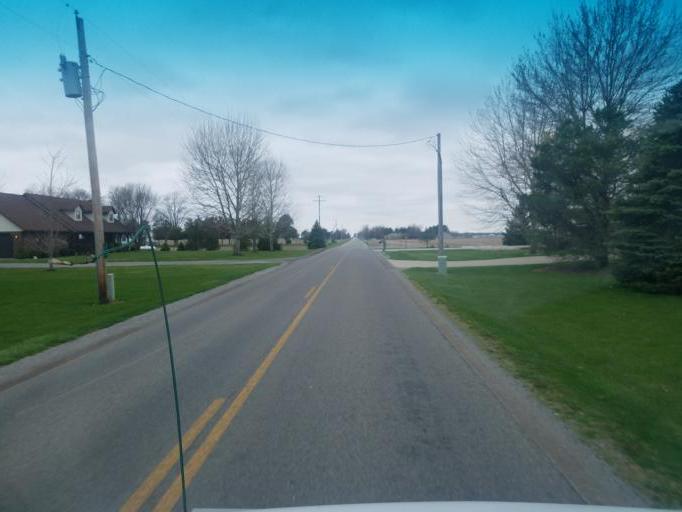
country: US
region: Ohio
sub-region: Allen County
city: Delphos
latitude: 40.9179
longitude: -84.3592
